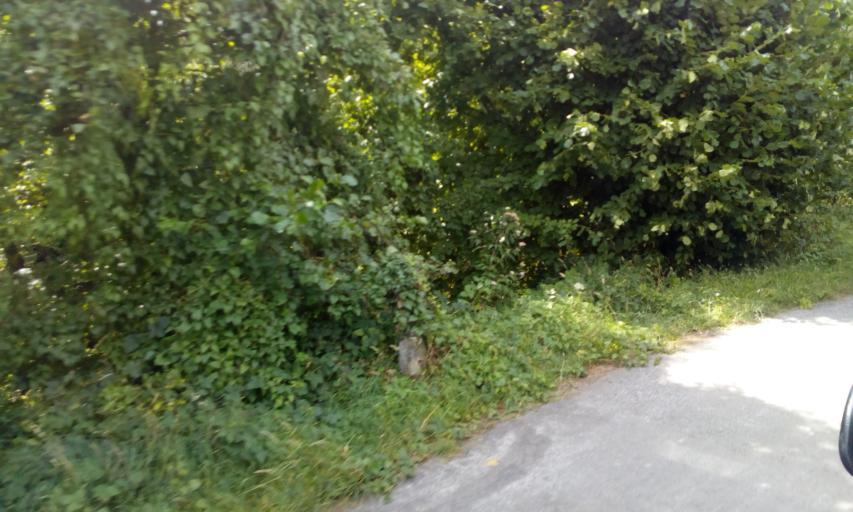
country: BE
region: Wallonia
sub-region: Province du Luxembourg
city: Tellin
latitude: 50.1223
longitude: 5.1892
